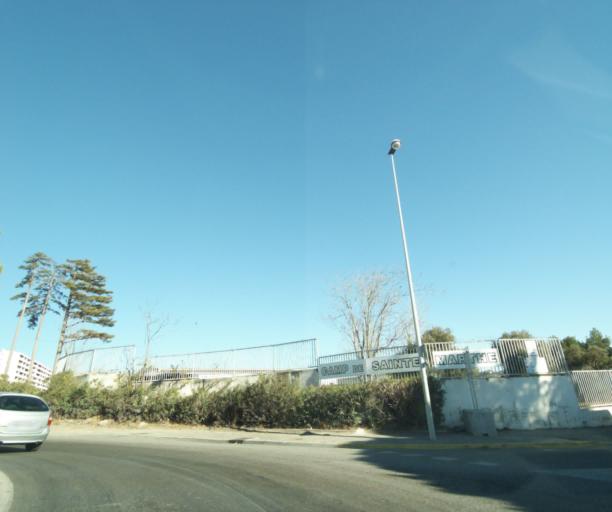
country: FR
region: Provence-Alpes-Cote d'Azur
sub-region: Departement des Bouches-du-Rhone
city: Marseille 14
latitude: 43.3368
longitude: 5.3859
